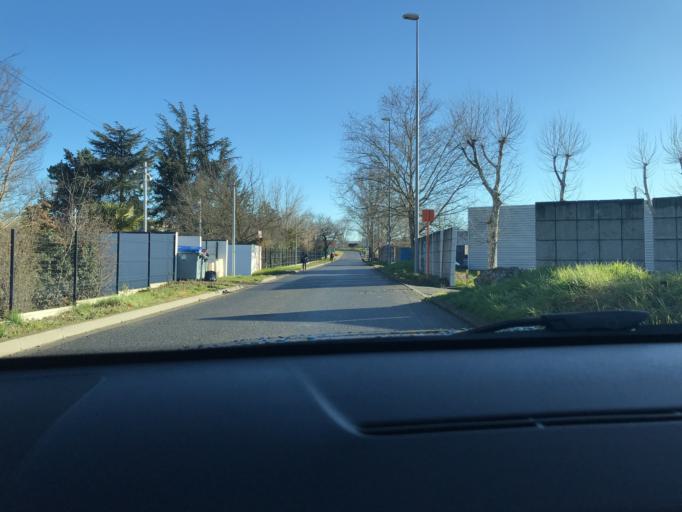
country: FR
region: Midi-Pyrenees
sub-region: Departement de la Haute-Garonne
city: Ramonville-Saint-Agne
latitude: 43.5527
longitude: 1.5029
